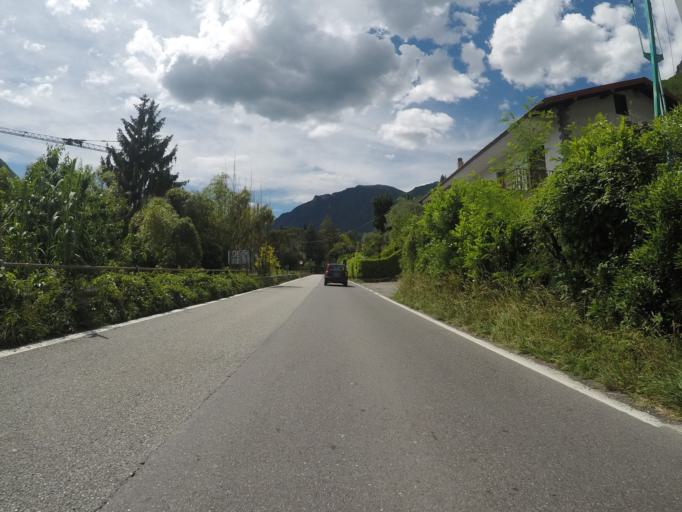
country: IT
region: Lombardy
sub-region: Provincia di Como
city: Osteno
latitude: 46.0243
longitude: 9.0765
